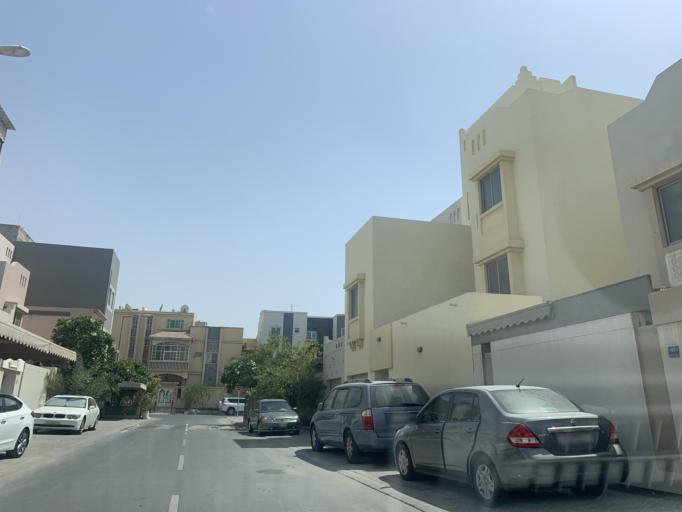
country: BH
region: Central Governorate
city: Madinat Hamad
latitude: 26.1473
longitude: 50.4974
